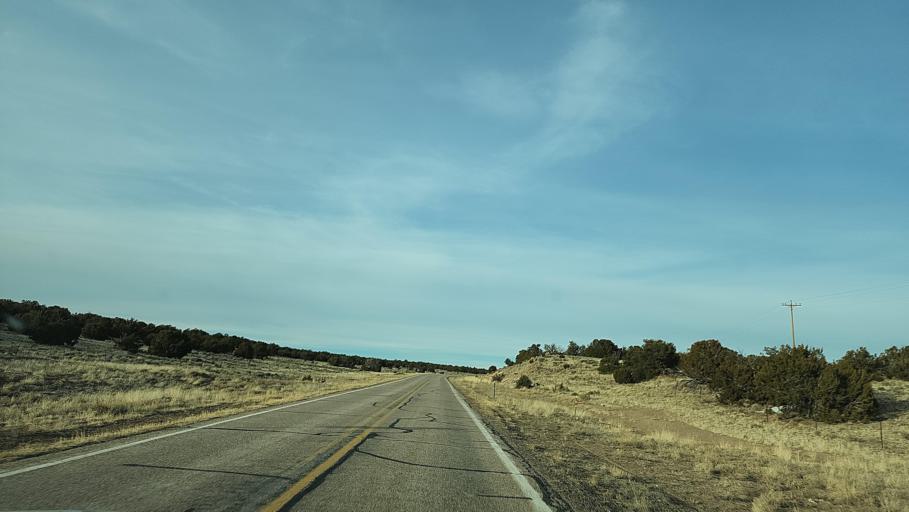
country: US
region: New Mexico
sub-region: Catron County
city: Reserve
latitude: 34.4066
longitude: -108.4369
